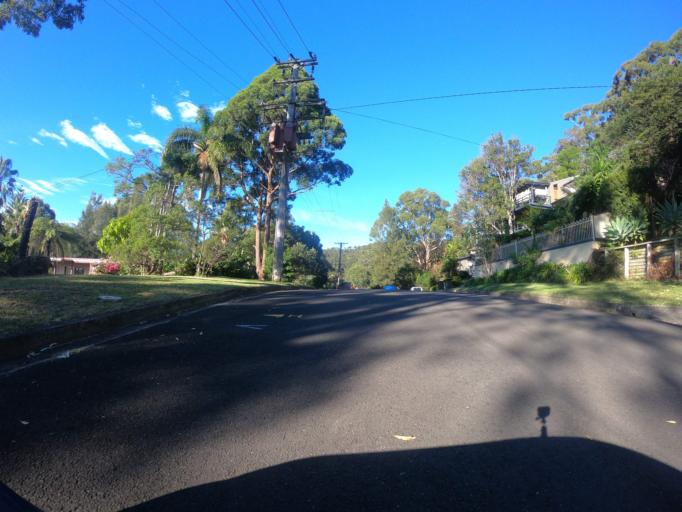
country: AU
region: New South Wales
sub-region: Wollongong
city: Bulli
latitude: -34.3239
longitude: 150.9044
